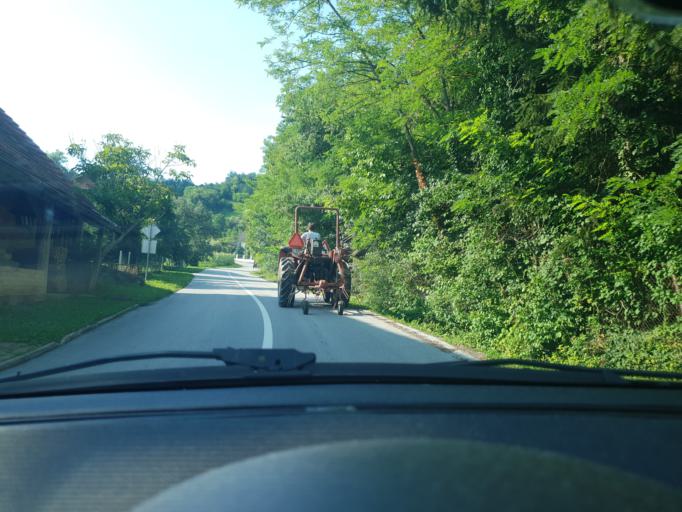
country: HR
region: Krapinsko-Zagorska
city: Pregrada
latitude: 46.0696
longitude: 15.7934
